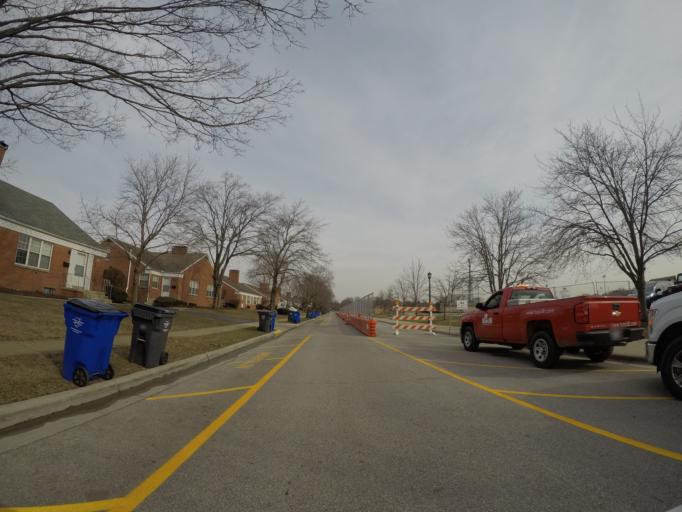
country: US
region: Ohio
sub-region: Franklin County
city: Upper Arlington
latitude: 40.0160
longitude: -83.0564
